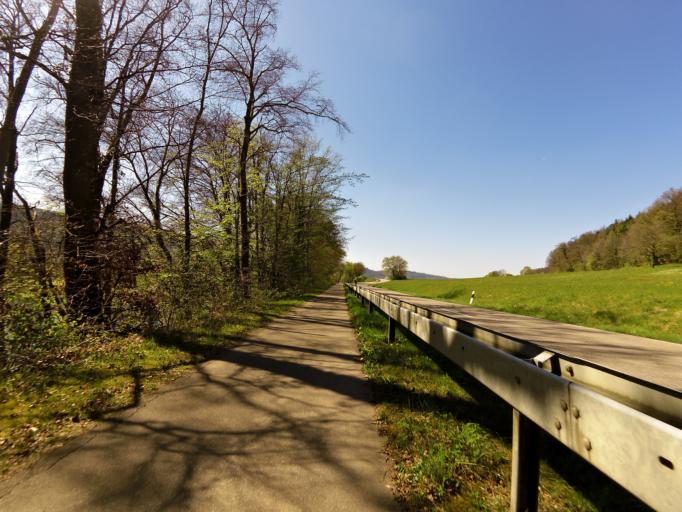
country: CH
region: Aargau
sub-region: Bezirk Zurzach
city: Bad Zurzach
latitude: 47.5714
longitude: 8.3507
